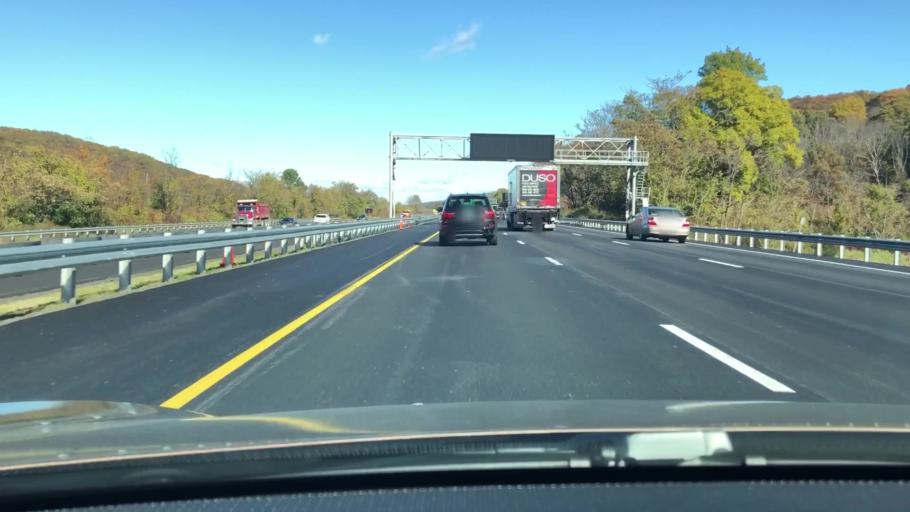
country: US
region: New York
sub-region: Orange County
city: Harriman
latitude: 41.2772
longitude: -74.1478
